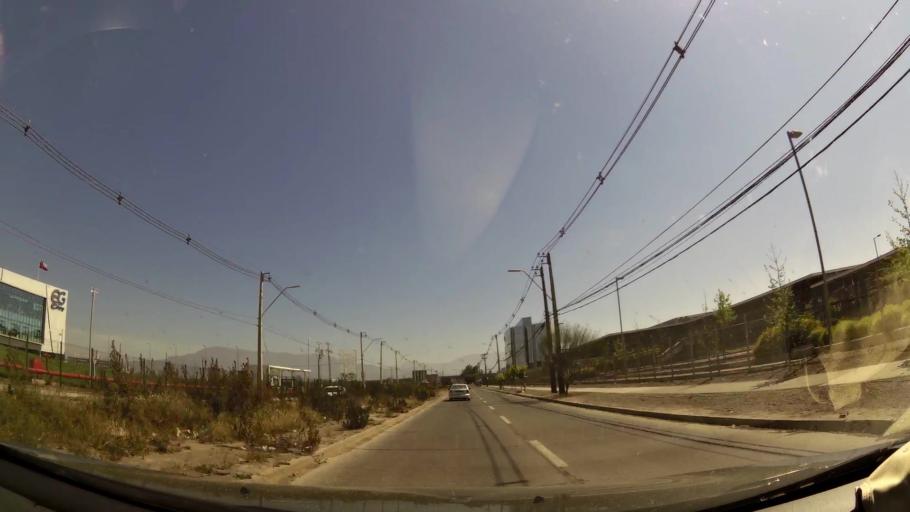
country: CL
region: Santiago Metropolitan
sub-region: Provincia de Santiago
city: Lo Prado
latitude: -33.3956
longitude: -70.7659
